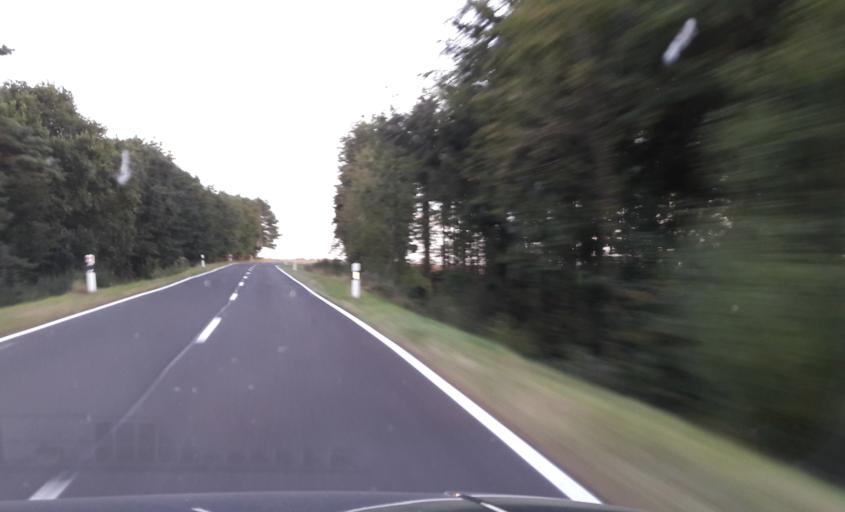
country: DE
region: Rheinland-Pfalz
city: Bengel
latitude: 50.0111
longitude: 7.0883
